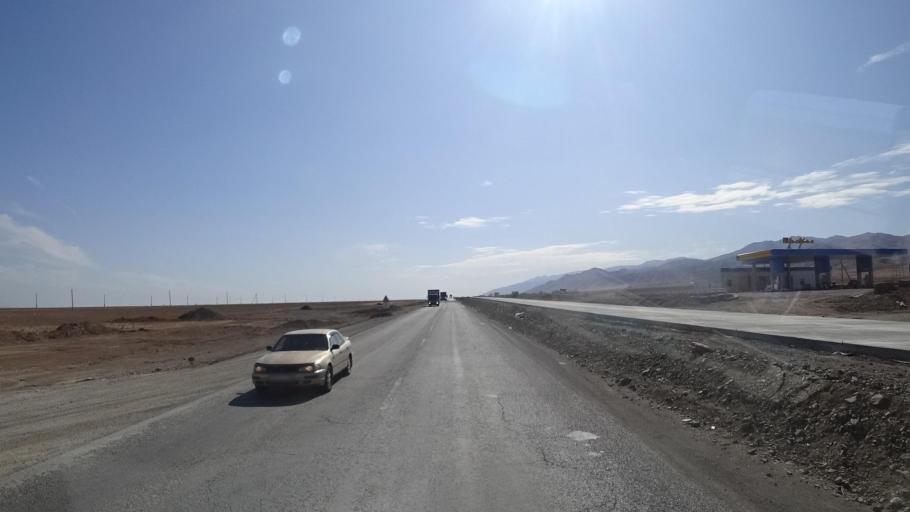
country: KG
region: Chuy
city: Ivanovka
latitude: 43.3998
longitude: 75.1155
